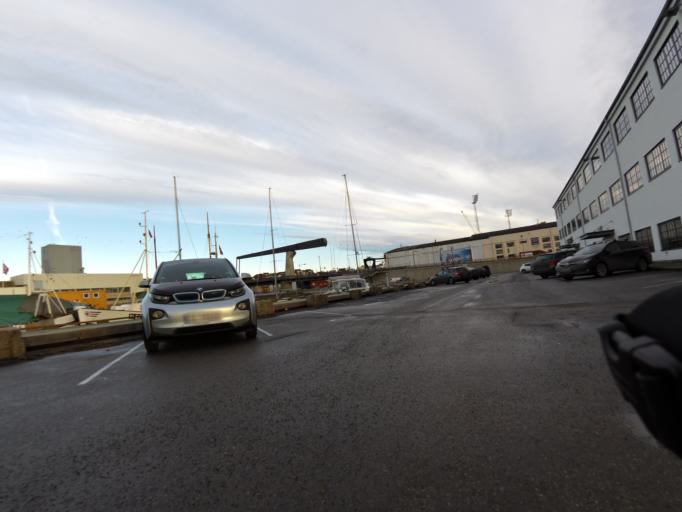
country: NO
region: Ostfold
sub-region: Fredrikstad
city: Fredrikstad
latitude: 59.2138
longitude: 10.9219
